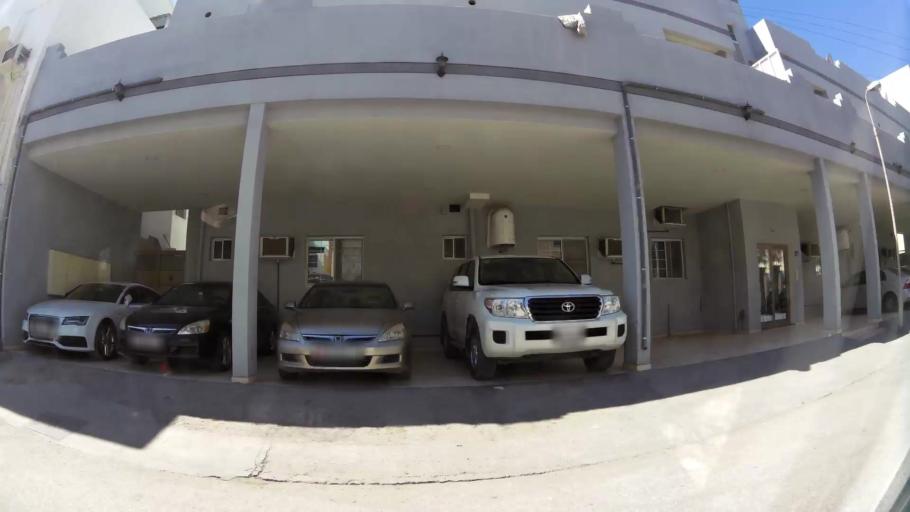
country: BH
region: Muharraq
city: Al Muharraq
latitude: 26.2822
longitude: 50.6244
